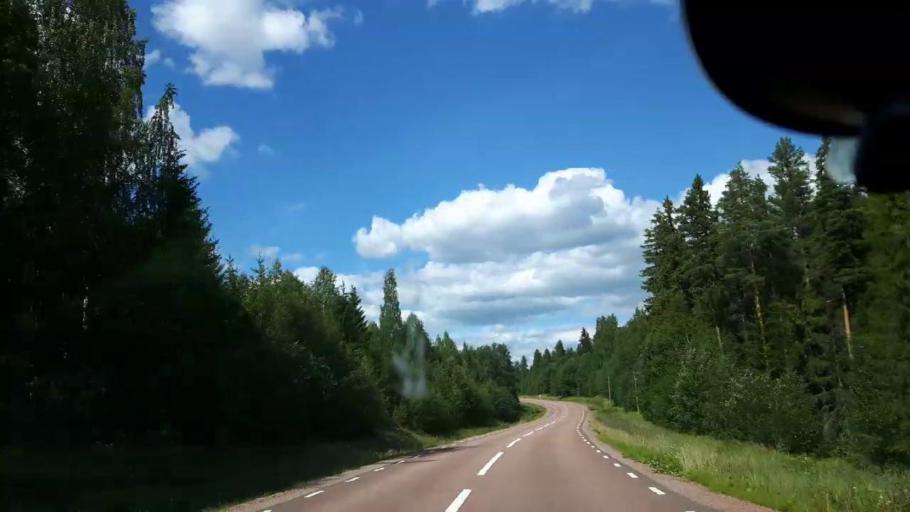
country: SE
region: Jaemtland
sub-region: Ragunda Kommun
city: Hammarstrand
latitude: 63.0300
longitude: 16.5234
